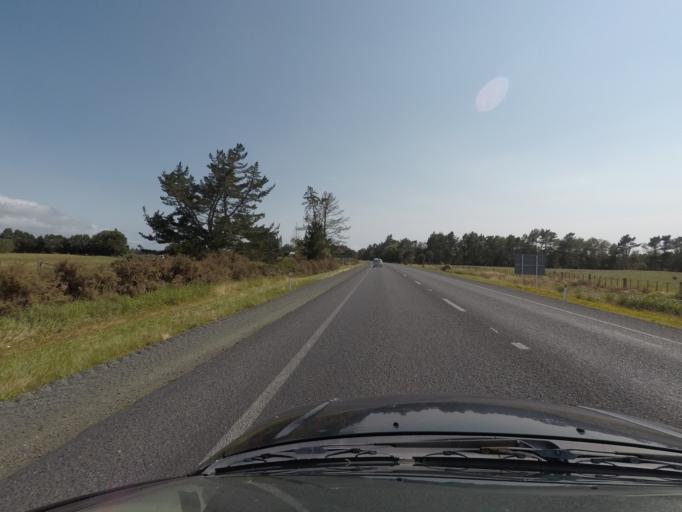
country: NZ
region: Northland
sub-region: Whangarei
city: Ruakaka
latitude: -35.9613
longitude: 174.4481
